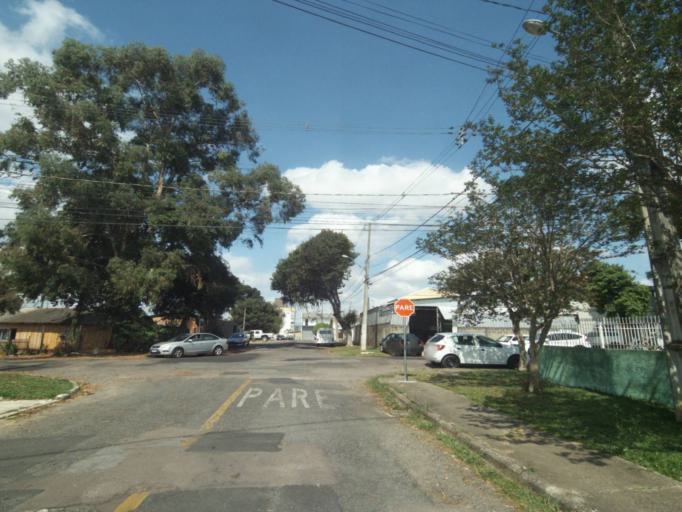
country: BR
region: Parana
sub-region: Curitiba
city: Curitiba
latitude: -25.4964
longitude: -49.3058
